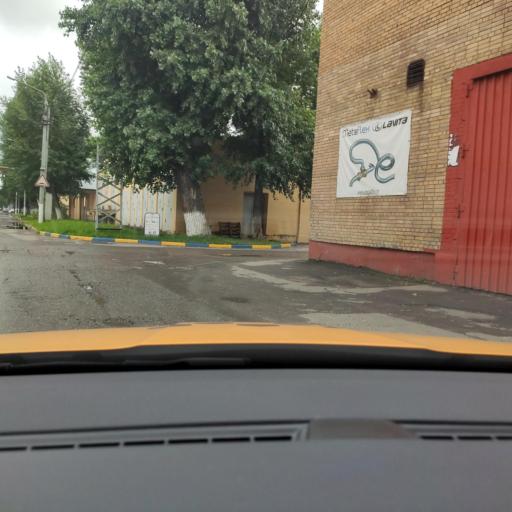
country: RU
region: Moskovskaya
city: Kozhukhovo
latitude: 55.7002
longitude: 37.6911
